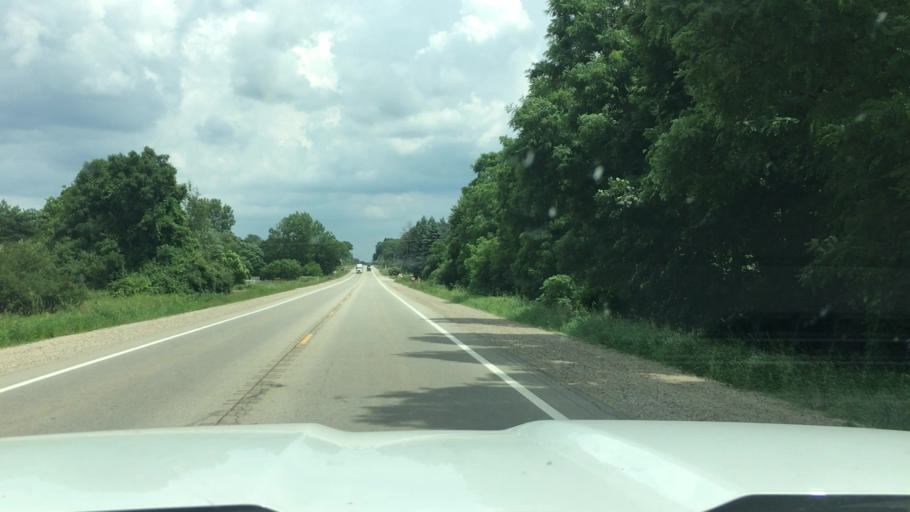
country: US
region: Michigan
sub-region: Kent County
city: Cedar Springs
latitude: 43.1763
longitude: -85.4087
